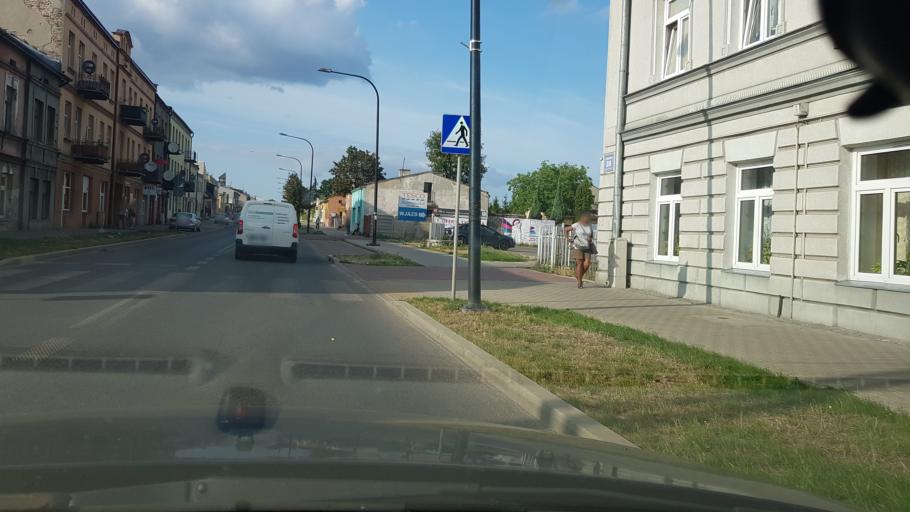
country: PL
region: Lodz Voivodeship
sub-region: Powiat tomaszowski
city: Tomaszow Mazowiecki
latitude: 51.5360
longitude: 20.0098
